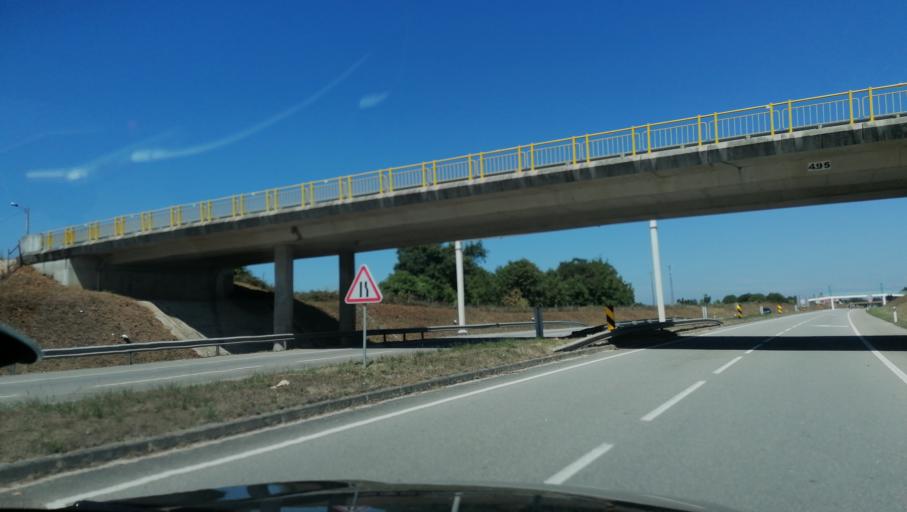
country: PT
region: Aveiro
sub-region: Agueda
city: Agueda
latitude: 40.5584
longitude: -8.4753
